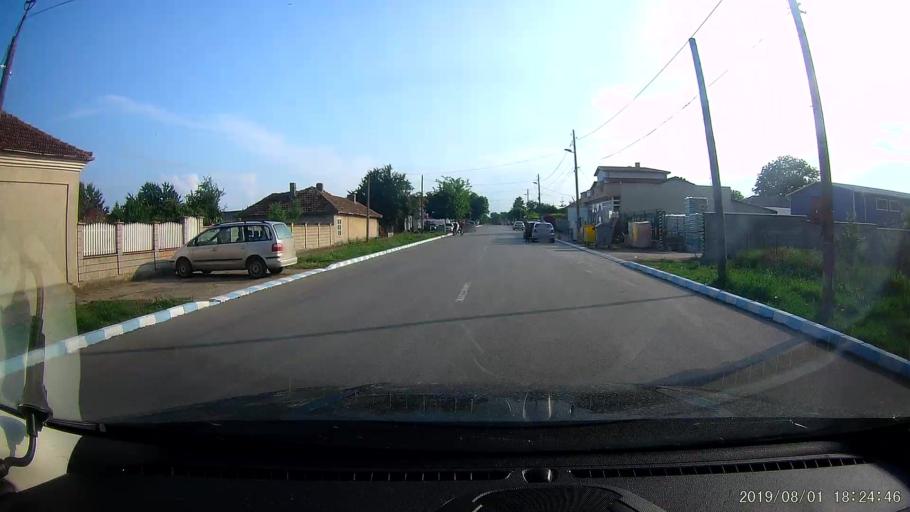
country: BG
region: Shumen
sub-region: Obshtina Venets
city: Venets
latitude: 43.6225
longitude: 27.0034
